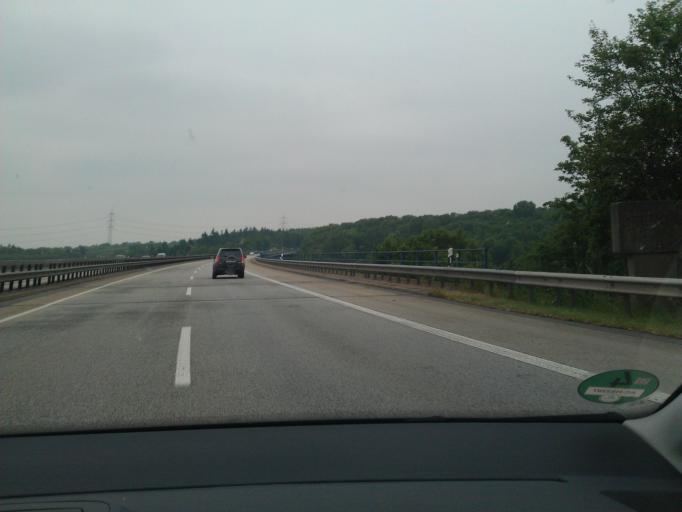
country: DE
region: Rheinland-Pfalz
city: Bassenheim
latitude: 50.3661
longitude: 7.4670
